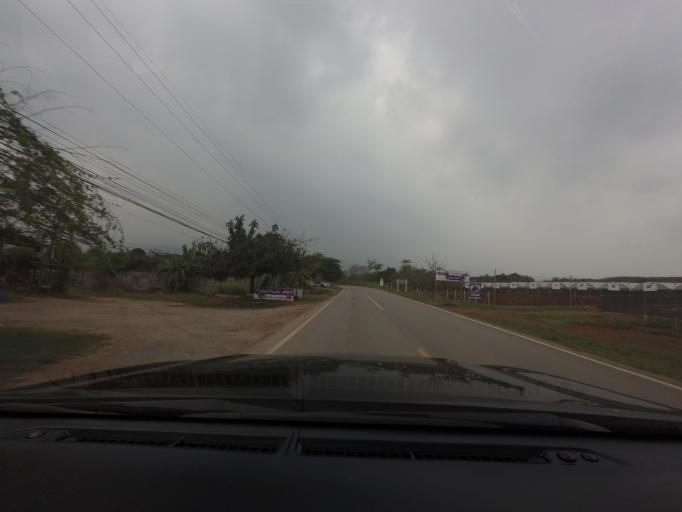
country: TH
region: Nakhon Ratchasima
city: Wang Nam Khiao
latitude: 14.4809
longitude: 101.5962
